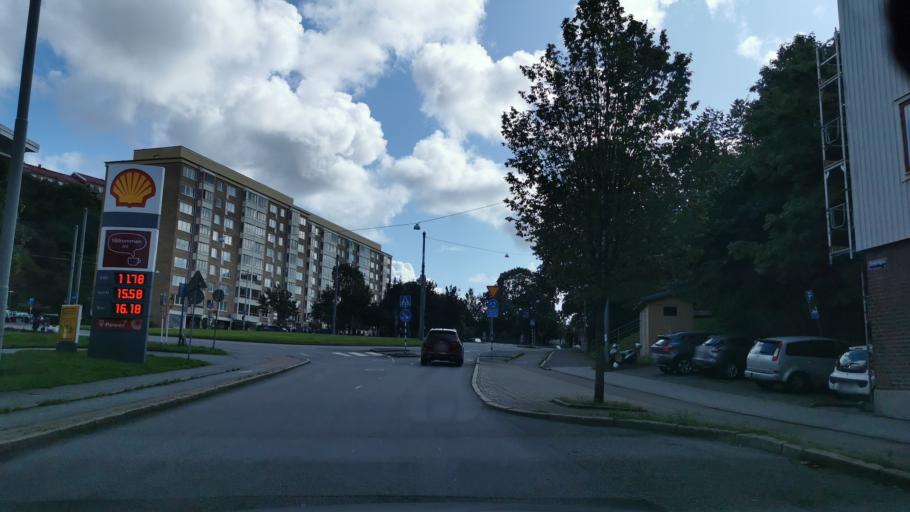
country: SE
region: Vaestra Goetaland
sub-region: Goteborg
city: Majorna
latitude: 57.6942
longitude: 11.9353
